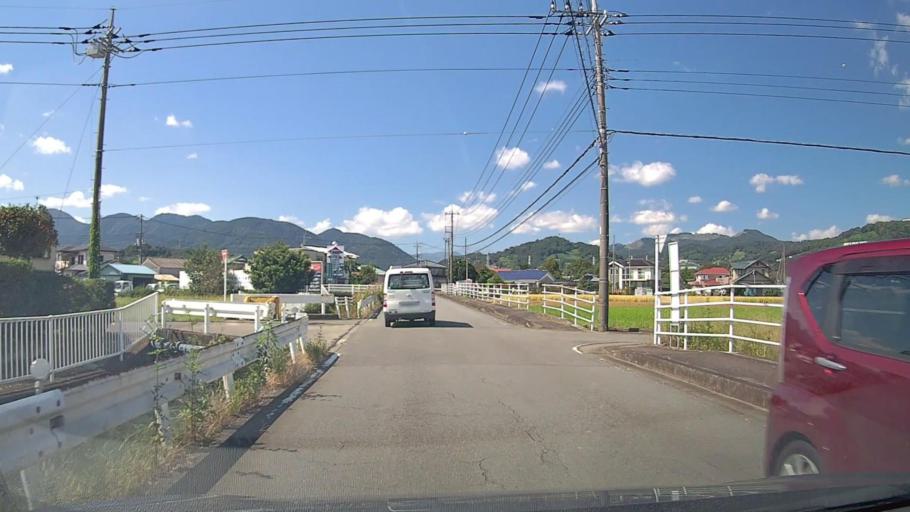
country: JP
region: Kanagawa
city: Odawara
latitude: 35.3463
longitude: 139.1056
